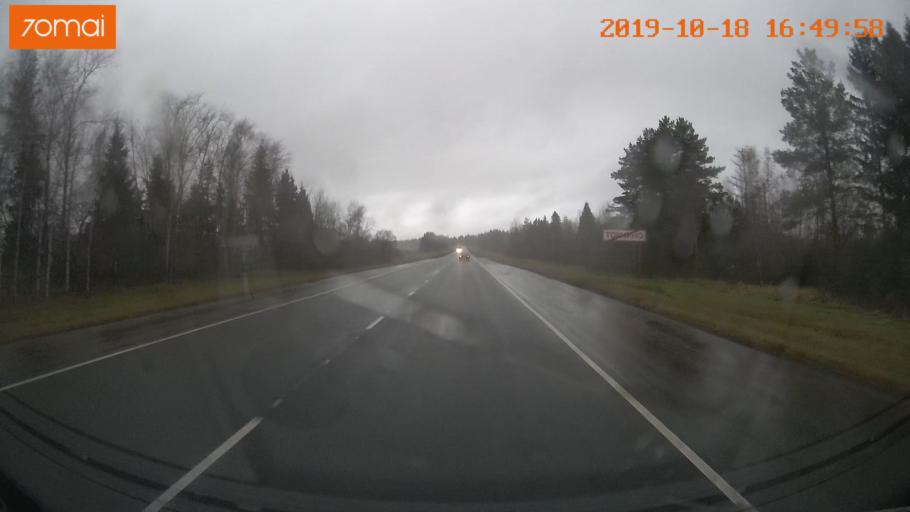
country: RU
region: Vladimir
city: Kideksha
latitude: 56.5647
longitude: 40.5509
